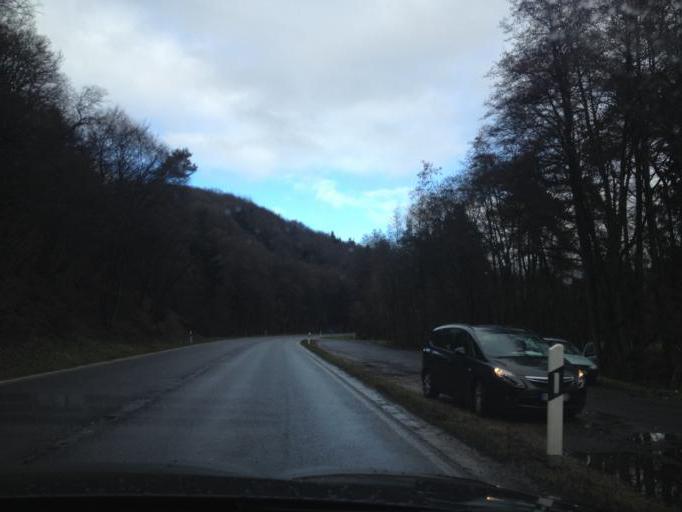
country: DE
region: Rheinland-Pfalz
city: Ellweiler
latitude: 49.6189
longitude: 7.1588
